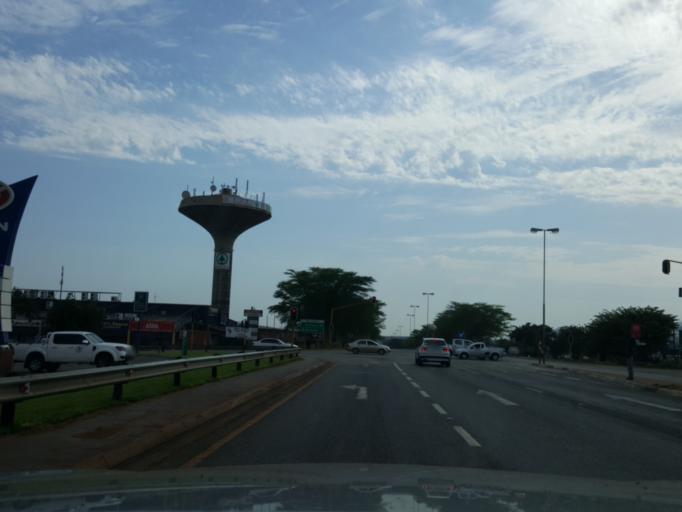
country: SZ
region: Hhohho
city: Ntfonjeni
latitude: -25.4997
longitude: 31.5083
